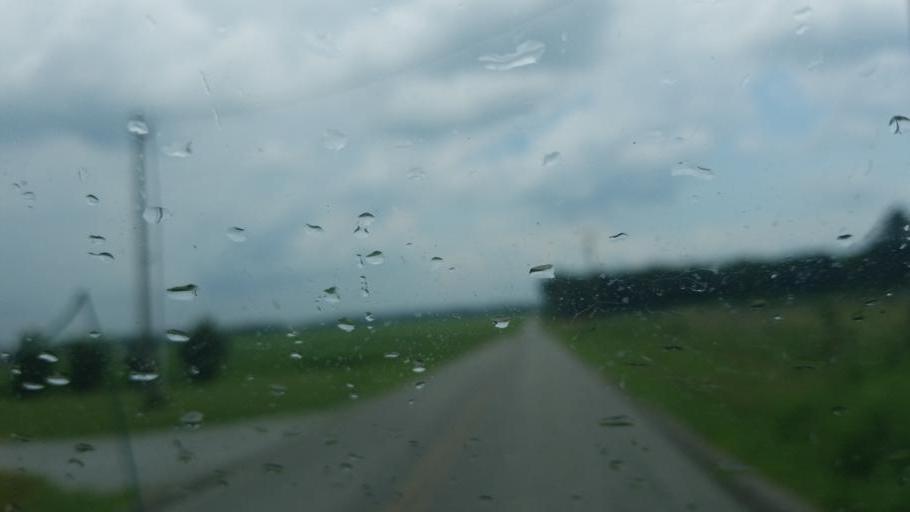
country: US
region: Ohio
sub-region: Wayne County
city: West Salem
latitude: 40.8579
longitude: -82.0890
